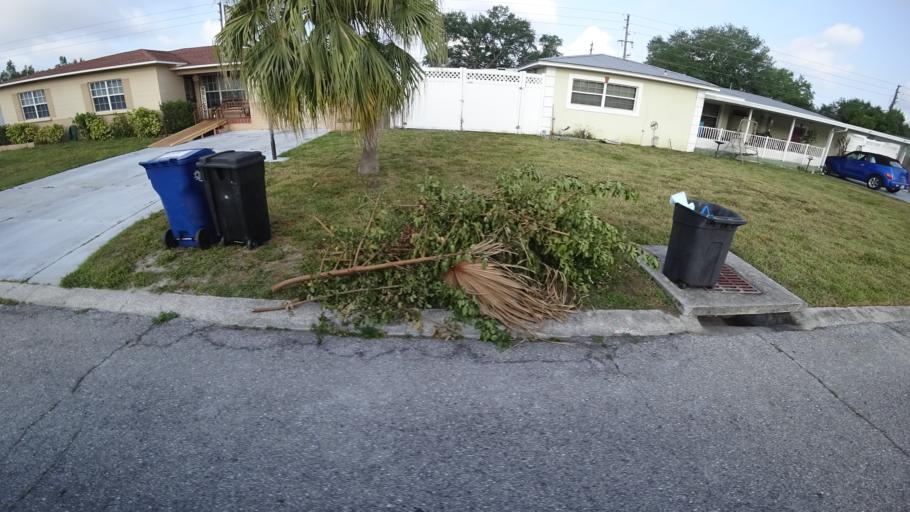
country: US
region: Florida
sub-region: Manatee County
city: South Bradenton
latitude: 27.4566
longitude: -82.5738
